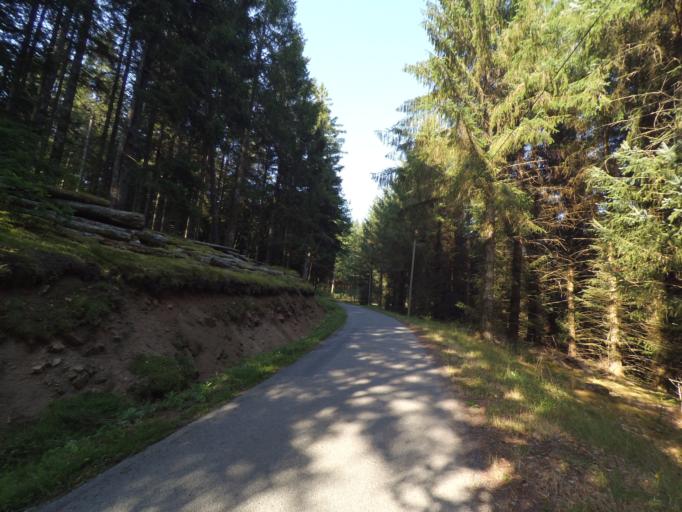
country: FR
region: Limousin
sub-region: Departement de la Correze
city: Bugeat
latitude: 45.6834
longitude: 2.0264
